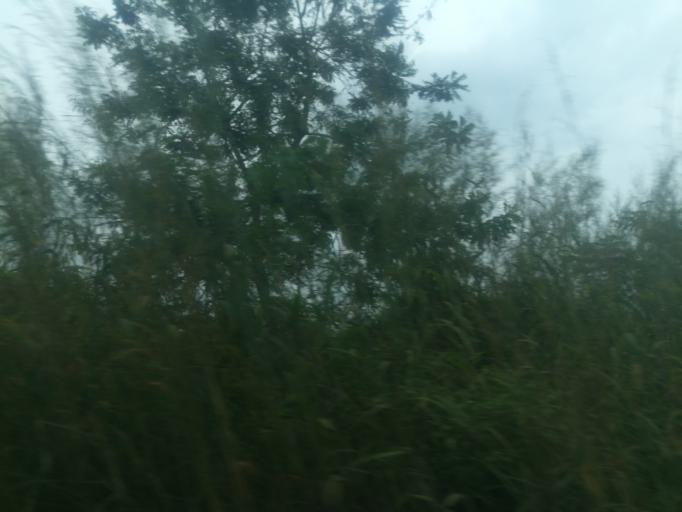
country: NG
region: Ogun
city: Ayetoro
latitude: 7.1106
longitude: 3.1304
